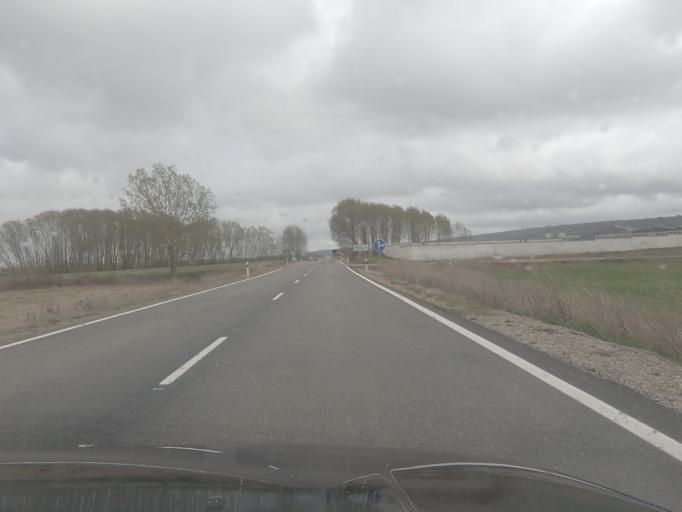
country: ES
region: Castille and Leon
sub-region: Provincia de Zamora
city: Pozuelo de Tabara
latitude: 41.7816
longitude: -5.8903
